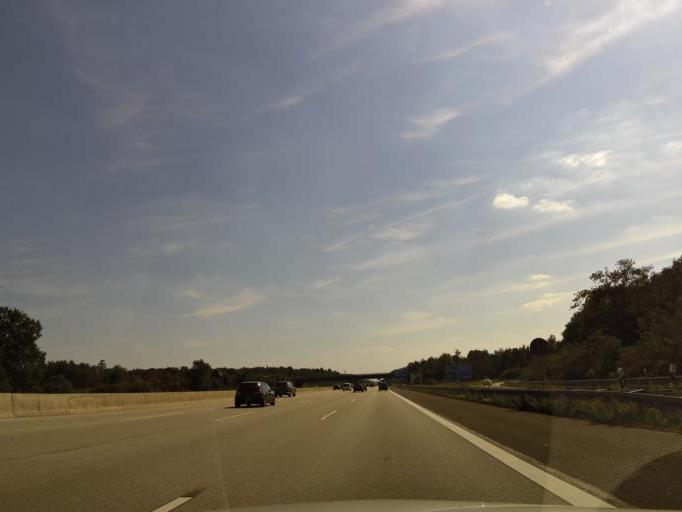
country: DE
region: Hesse
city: Morfelden-Walldorf
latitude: 49.9861
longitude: 8.6004
